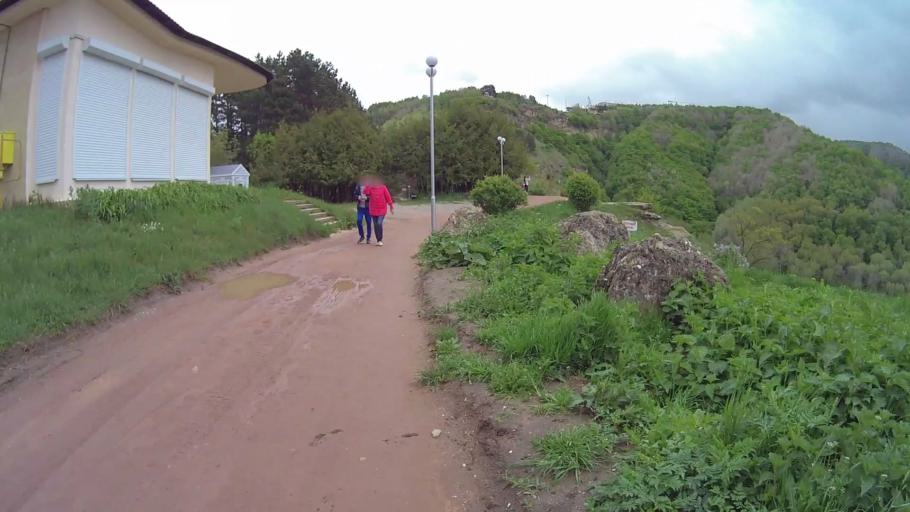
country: RU
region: Stavropol'skiy
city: Kislovodsk
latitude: 43.8997
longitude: 42.7504
